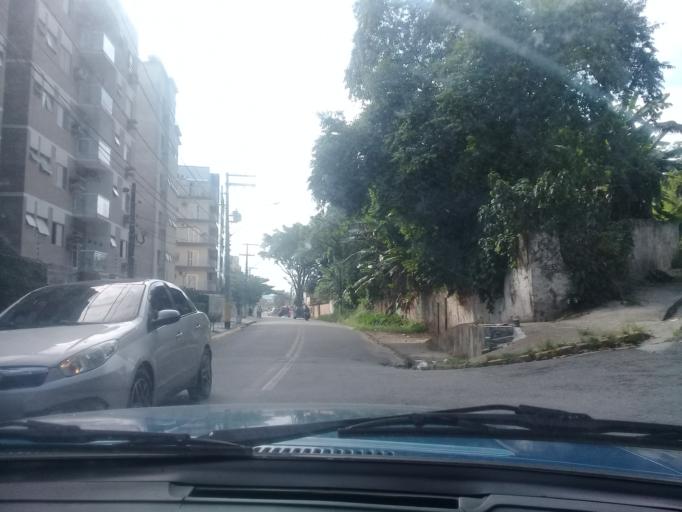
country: BR
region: Sao Paulo
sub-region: Guaruja
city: Guaruja
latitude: -24.0053
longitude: -46.2714
